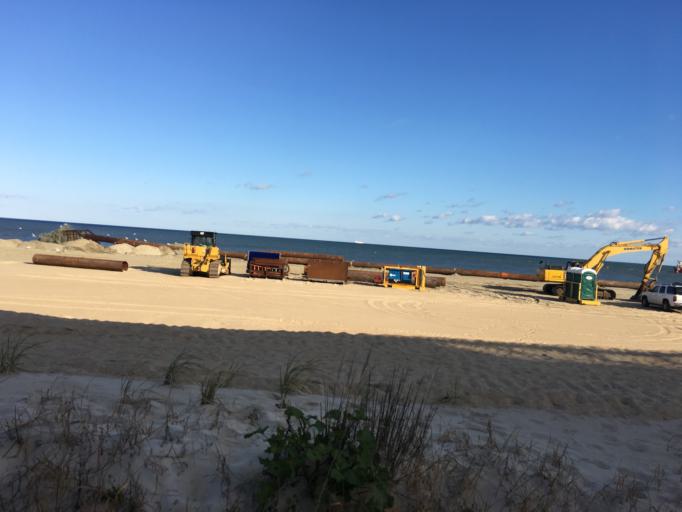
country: US
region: Delaware
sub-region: Sussex County
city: Rehoboth Beach
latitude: 38.7192
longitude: -75.0764
